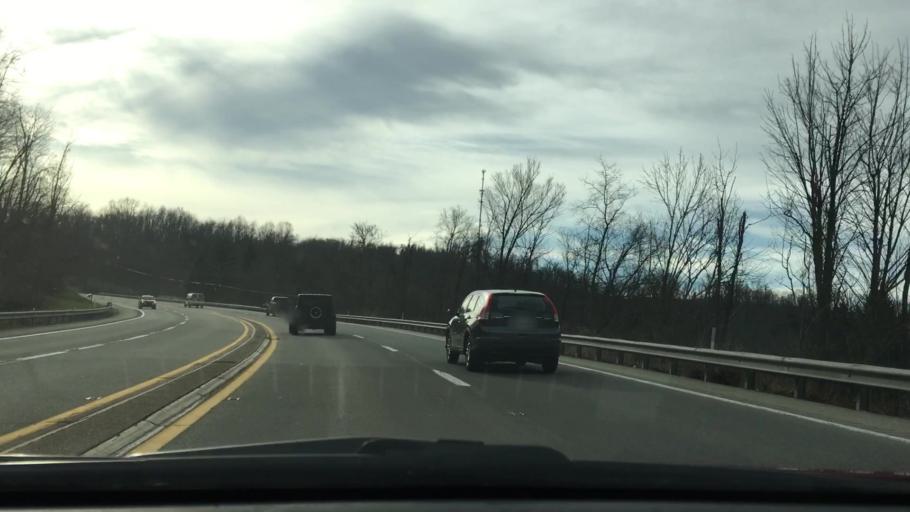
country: US
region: Pennsylvania
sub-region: Fayette County
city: Perryopolis
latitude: 40.0270
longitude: -79.7717
